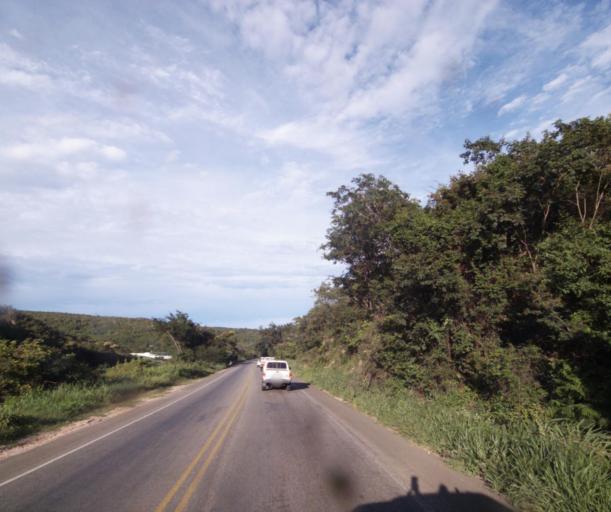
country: BR
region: Bahia
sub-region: Caetite
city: Caetite
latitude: -14.0626
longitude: -42.5131
